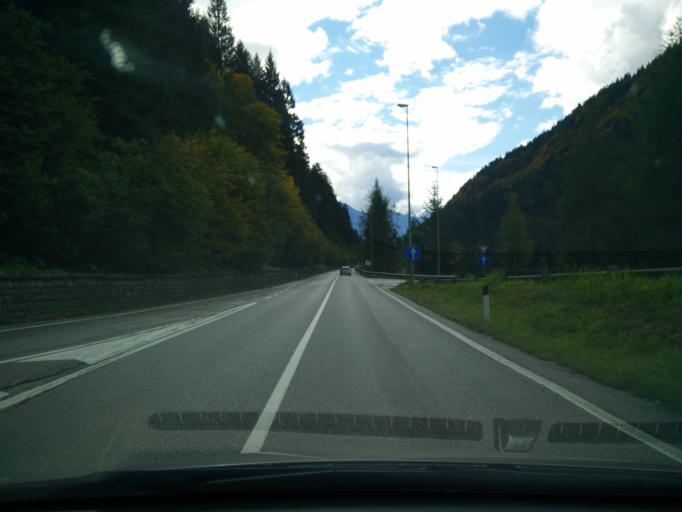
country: IT
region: Veneto
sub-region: Provincia di Belluno
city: Vigo di Cadore
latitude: 46.5314
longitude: 12.4693
